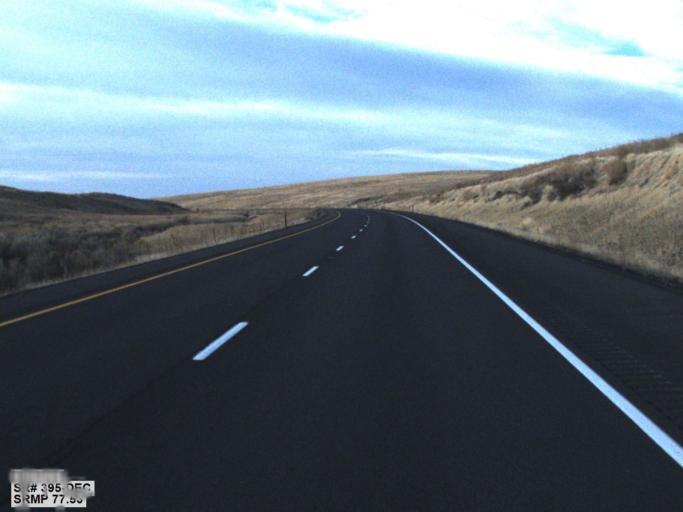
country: US
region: Washington
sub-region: Adams County
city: Ritzville
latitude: 46.9098
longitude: -118.6099
